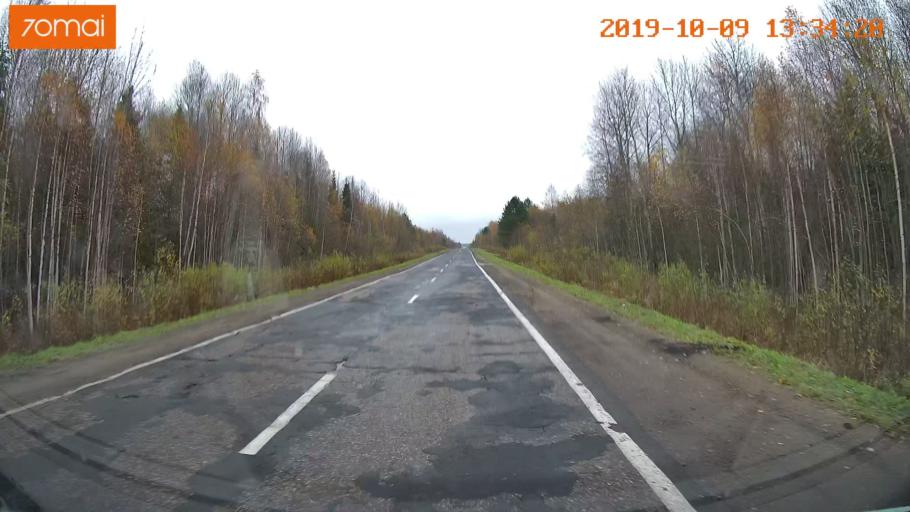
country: RU
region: Jaroslavl
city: Lyubim
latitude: 58.3297
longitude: 41.0596
